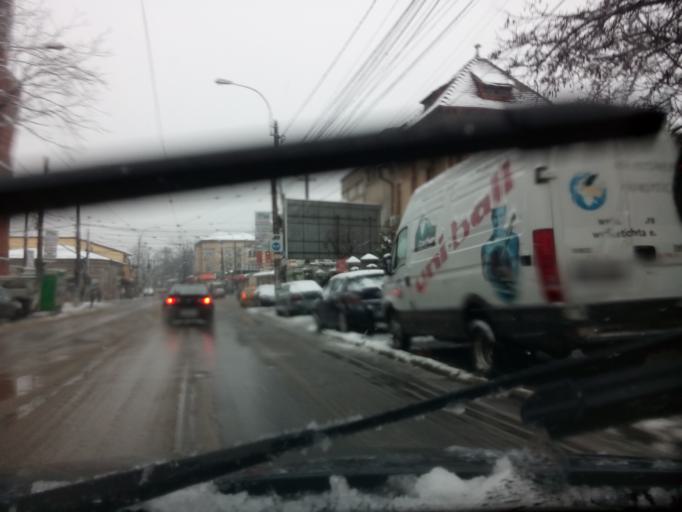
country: RO
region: Bucuresti
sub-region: Municipiul Bucuresti
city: Bucharest
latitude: 44.4329
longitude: 26.1218
